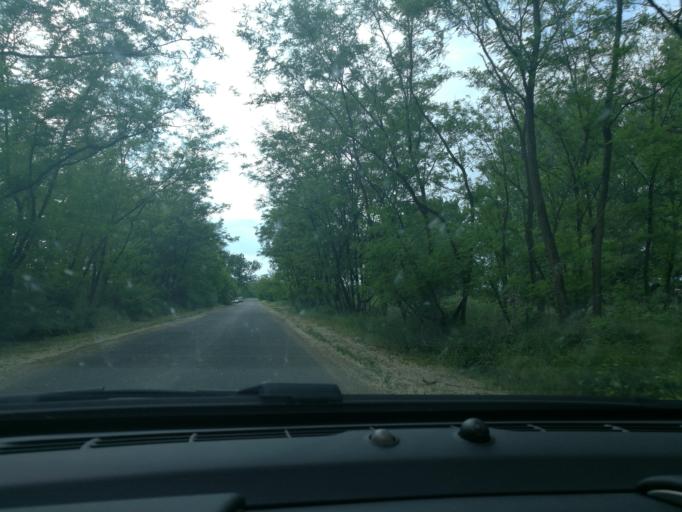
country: HU
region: Szabolcs-Szatmar-Bereg
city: Nyirpazony
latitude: 47.9295
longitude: 21.7982
